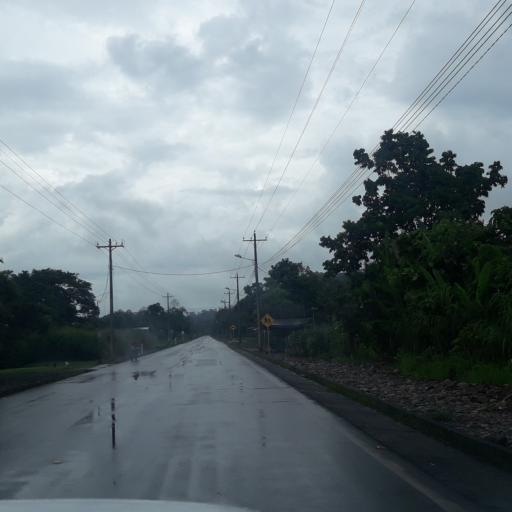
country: EC
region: Napo
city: Tena
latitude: -1.0658
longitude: -77.6429
